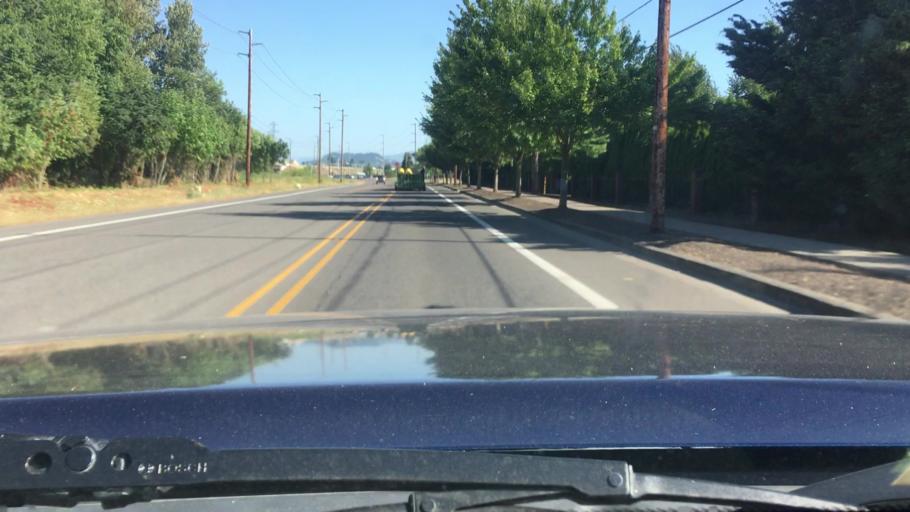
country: US
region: Oregon
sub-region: Lane County
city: Coburg
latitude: 44.0940
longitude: -123.0511
